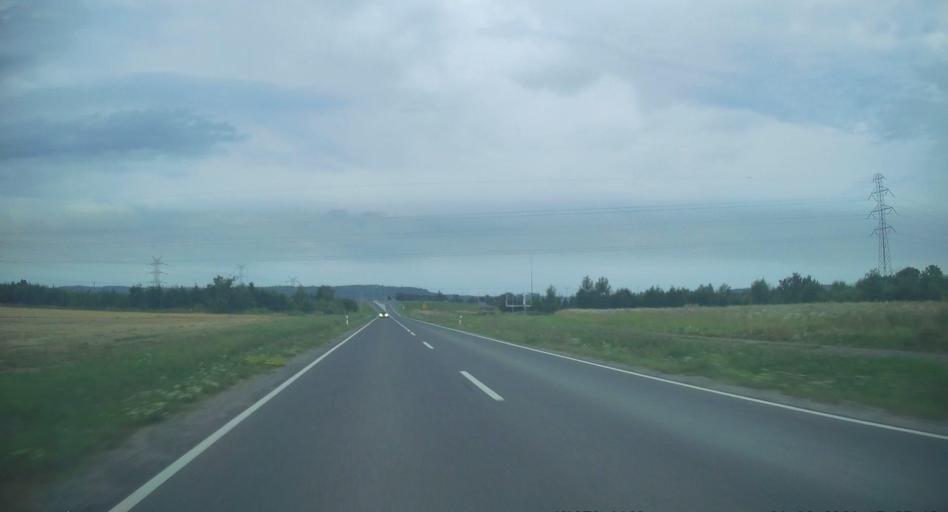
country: PL
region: Lesser Poland Voivodeship
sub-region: Powiat tarnowski
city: Wojnicz
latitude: 49.9676
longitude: 20.8471
